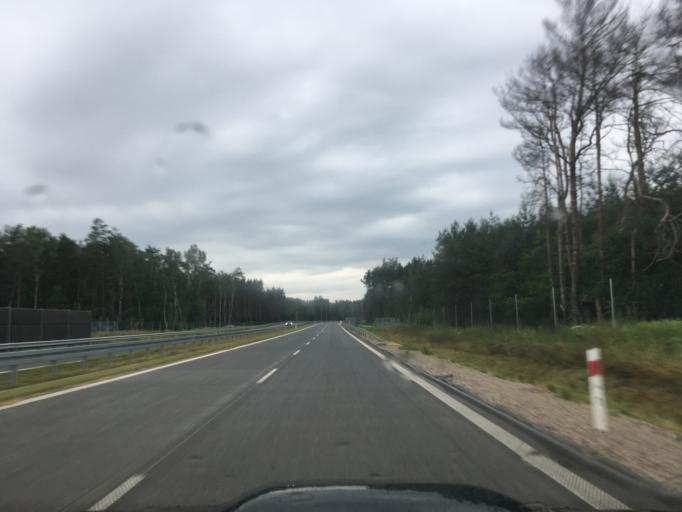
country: PL
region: Masovian Voivodeship
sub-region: Powiat piaseczynski
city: Gora Kalwaria
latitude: 51.9796
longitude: 21.1813
